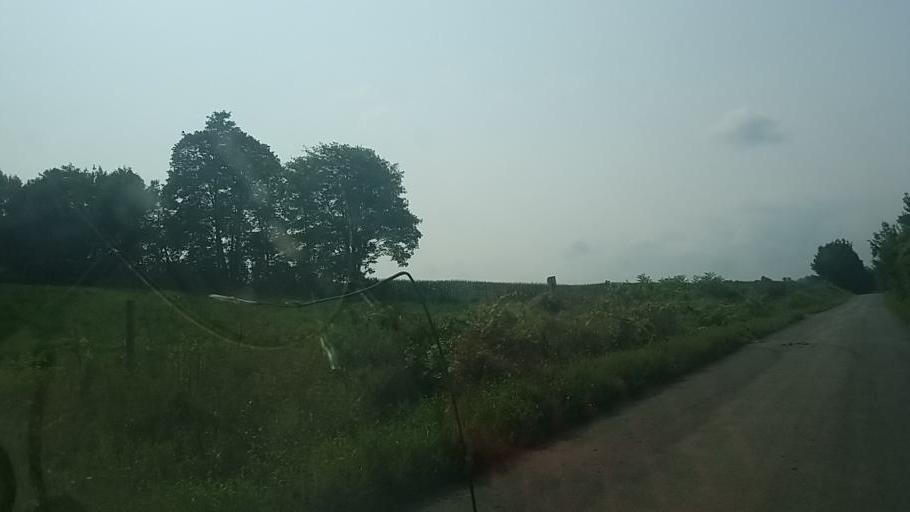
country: US
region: New York
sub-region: Montgomery County
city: Fonda
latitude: 42.9813
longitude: -74.4463
